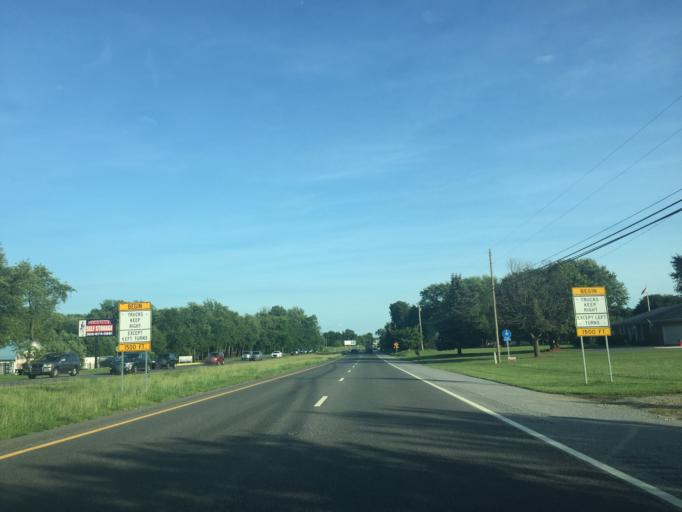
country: US
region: Delaware
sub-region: Kent County
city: Cheswold
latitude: 39.2335
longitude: -75.5818
